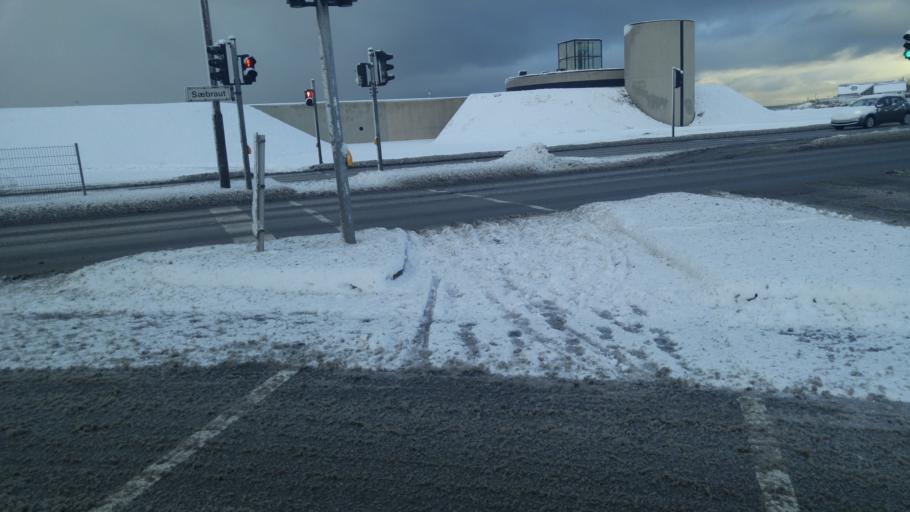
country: IS
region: Capital Region
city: Reykjavik
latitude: 64.1497
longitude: -21.8885
